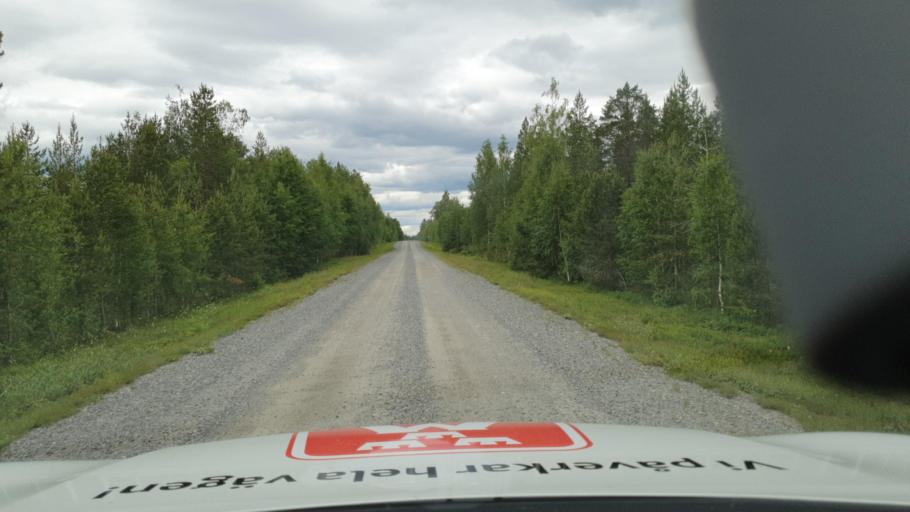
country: SE
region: Vaesterbotten
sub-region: Nordmalings Kommun
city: Nordmaling
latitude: 63.7418
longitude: 19.3860
